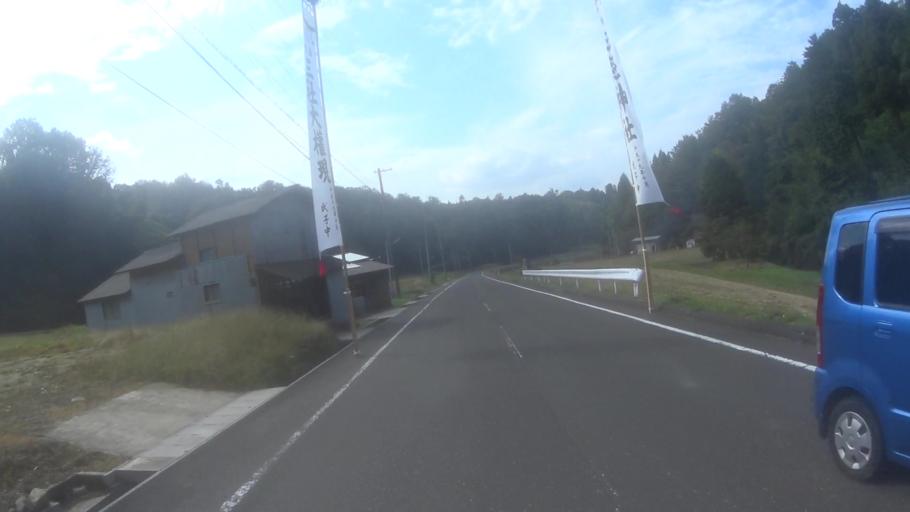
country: JP
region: Kyoto
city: Miyazu
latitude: 35.6033
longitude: 135.1592
